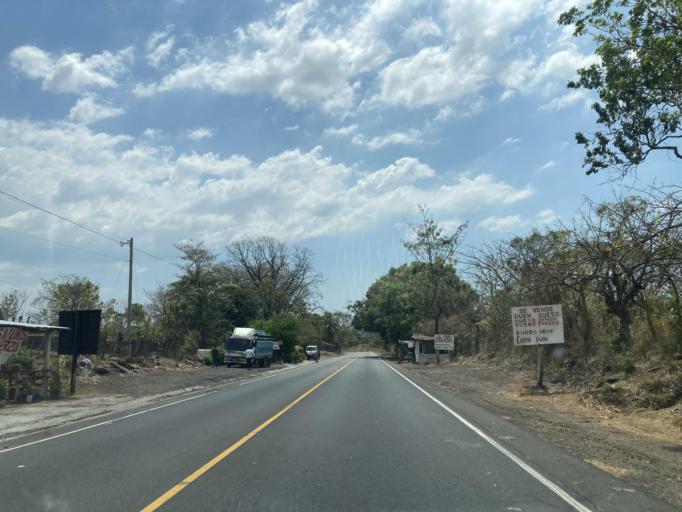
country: GT
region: Santa Rosa
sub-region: Municipio de Taxisco
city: Taxisco
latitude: 14.0726
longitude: -90.4749
